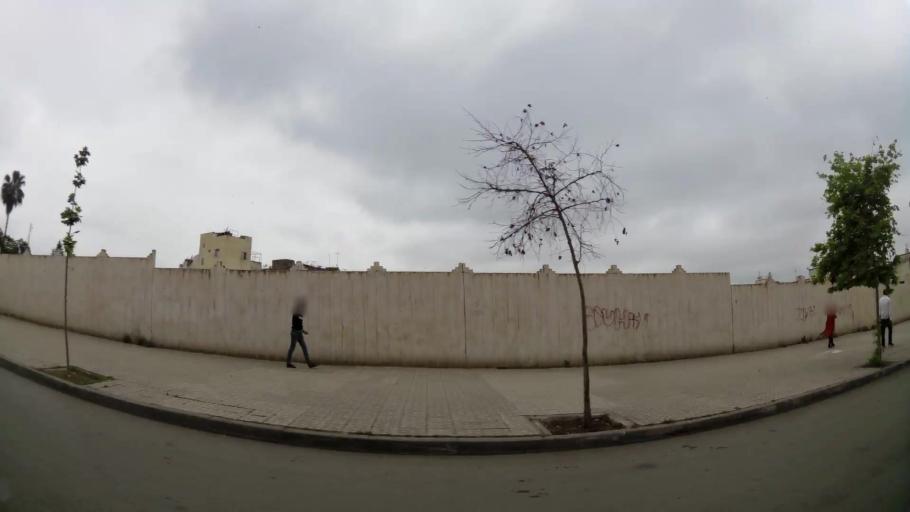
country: MA
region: Fes-Boulemane
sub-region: Fes
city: Fes
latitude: 34.0420
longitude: -5.0135
